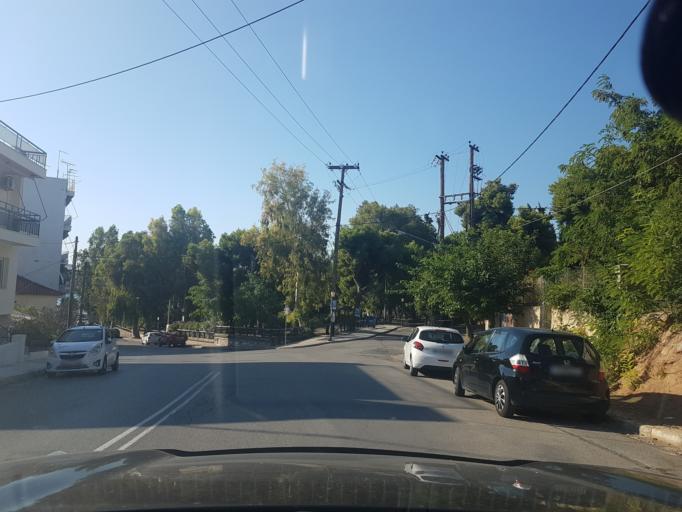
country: GR
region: Central Greece
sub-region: Nomos Evvoias
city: Chalkida
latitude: 38.4683
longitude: 23.5872
